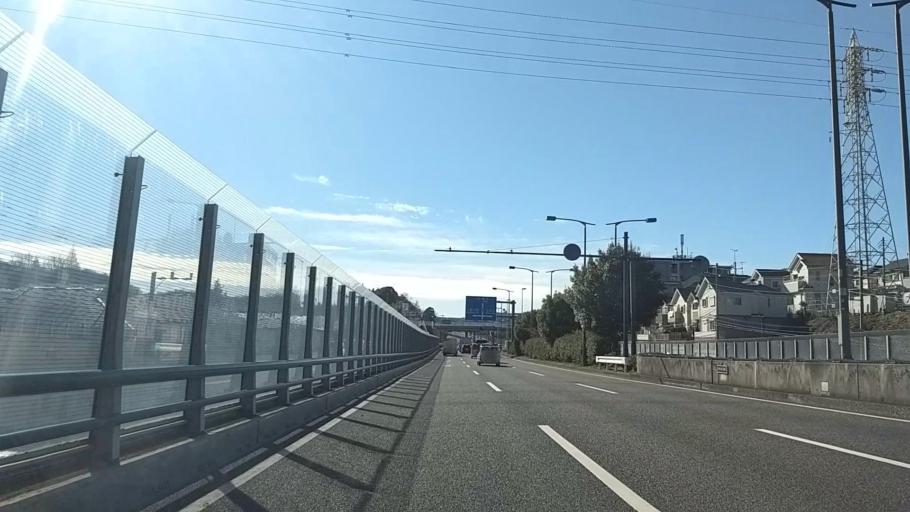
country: JP
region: Kanagawa
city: Yokohama
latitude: 35.4652
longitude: 139.5649
